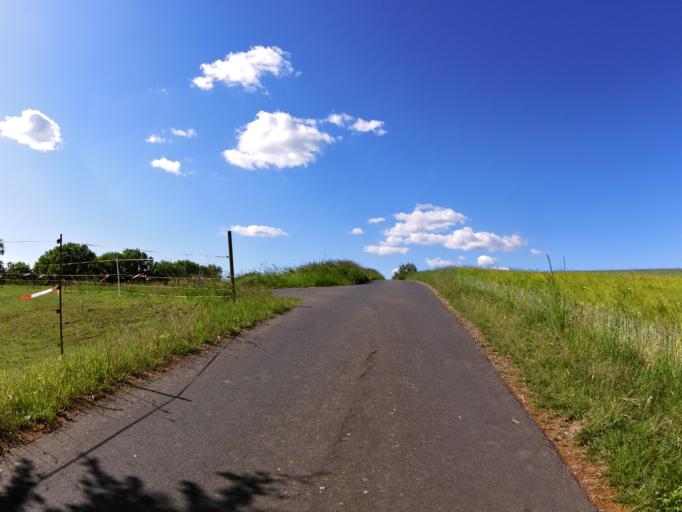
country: DE
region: Hesse
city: Philippsthal
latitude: 50.8283
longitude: 9.9972
